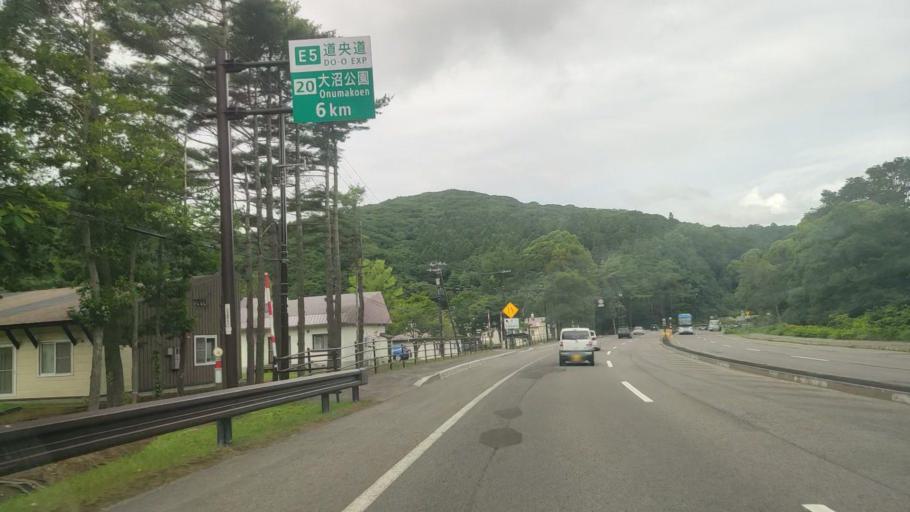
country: JP
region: Hokkaido
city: Nanae
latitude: 41.9605
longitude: 140.6475
